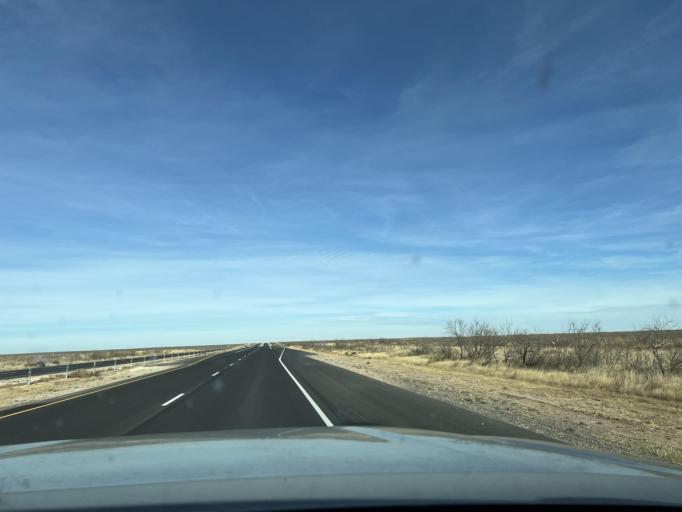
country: US
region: Texas
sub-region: Ector County
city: Gardendale
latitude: 32.0433
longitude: -102.4366
